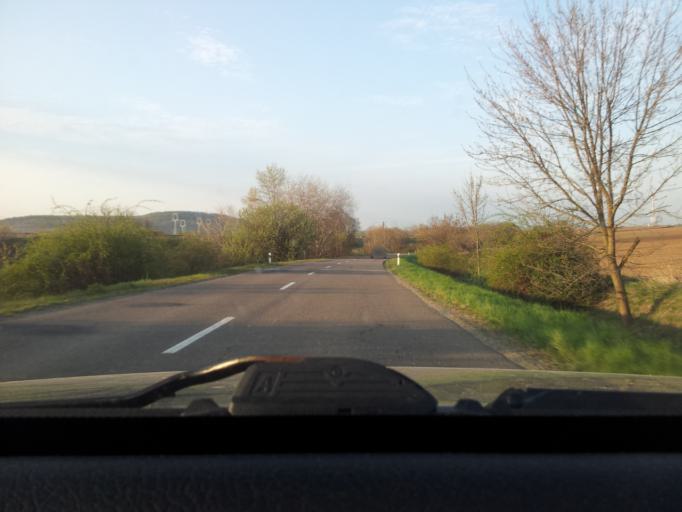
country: SK
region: Nitriansky
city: Tlmace
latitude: 48.2658
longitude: 18.4458
